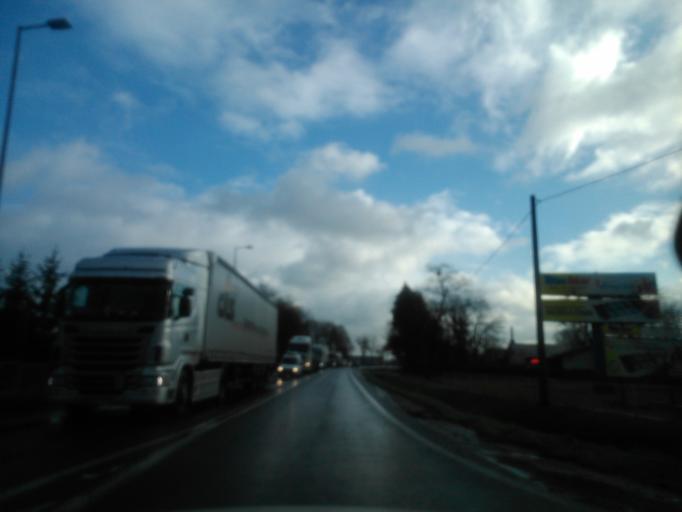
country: PL
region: Masovian Voivodeship
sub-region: Powiat sierpecki
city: Sierpc
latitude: 52.8613
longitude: 19.6756
